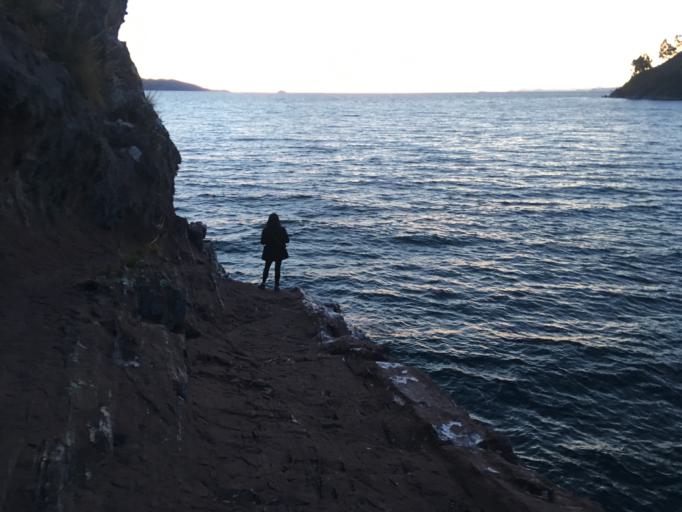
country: BO
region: La Paz
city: San Pablo
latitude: -16.2092
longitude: -68.8544
